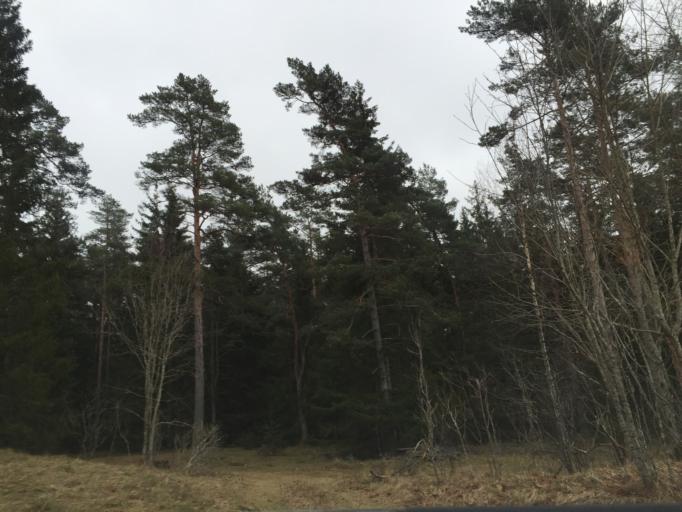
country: EE
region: Saare
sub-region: Kuressaare linn
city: Kuressaare
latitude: 58.3987
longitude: 22.2522
